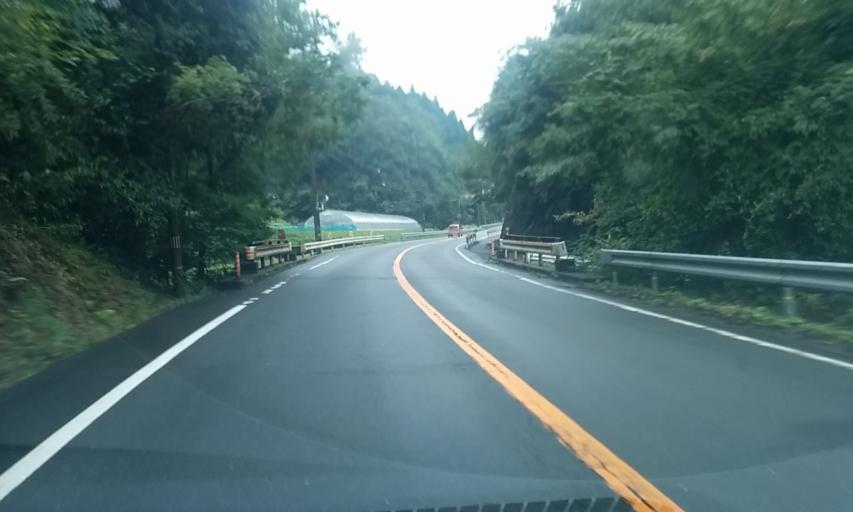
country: JP
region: Kyoto
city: Ayabe
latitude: 35.2287
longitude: 135.3354
